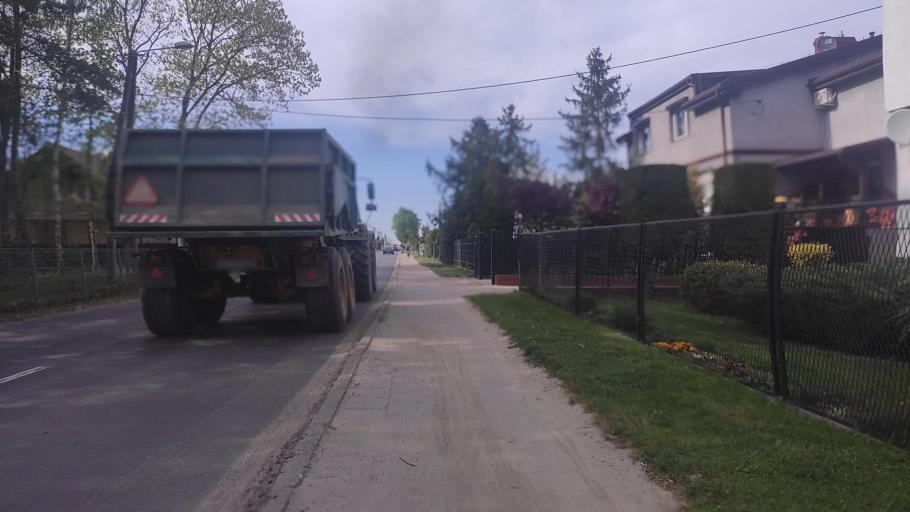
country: PL
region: Greater Poland Voivodeship
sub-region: Powiat poznanski
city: Kleszczewo
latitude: 52.3828
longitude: 17.1626
